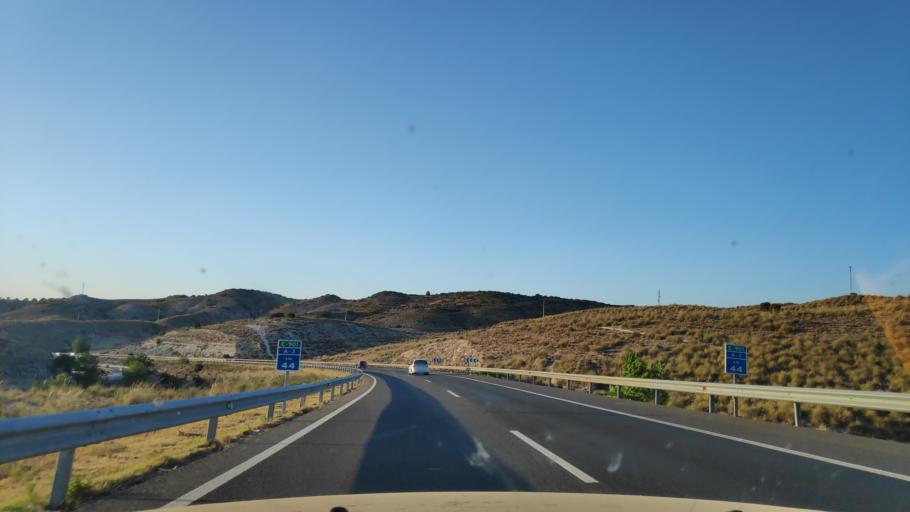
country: ES
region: Madrid
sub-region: Provincia de Madrid
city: Tielmes
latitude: 40.2040
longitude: -3.3142
